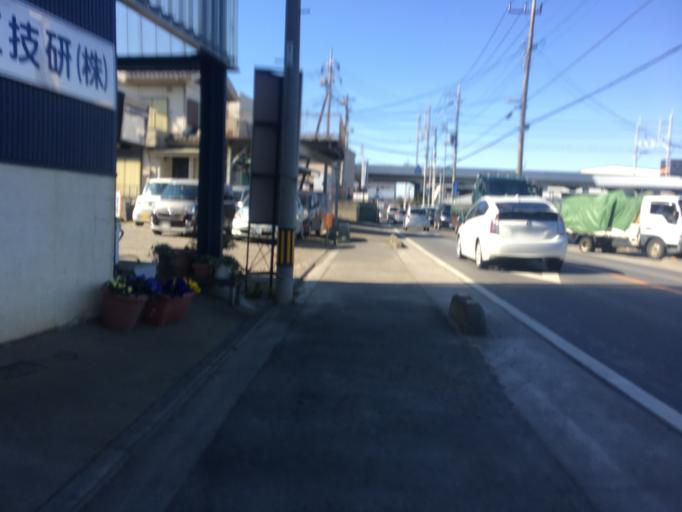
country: JP
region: Saitama
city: Asaka
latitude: 35.8262
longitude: 139.6099
